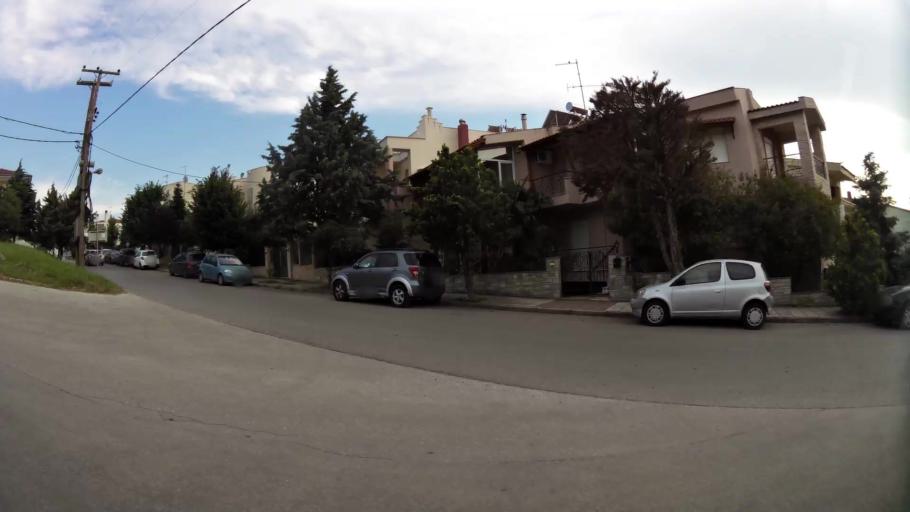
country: GR
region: Central Macedonia
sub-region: Nomos Thessalonikis
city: Pefka
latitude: 40.6632
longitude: 22.9846
